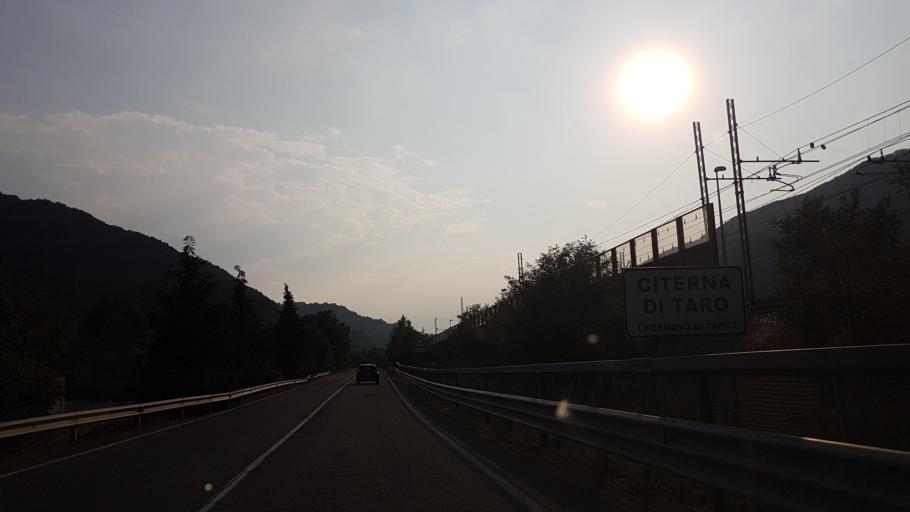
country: IT
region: Emilia-Romagna
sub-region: Provincia di Parma
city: Varano De' Melegari
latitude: 44.6380
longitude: 10.0378
